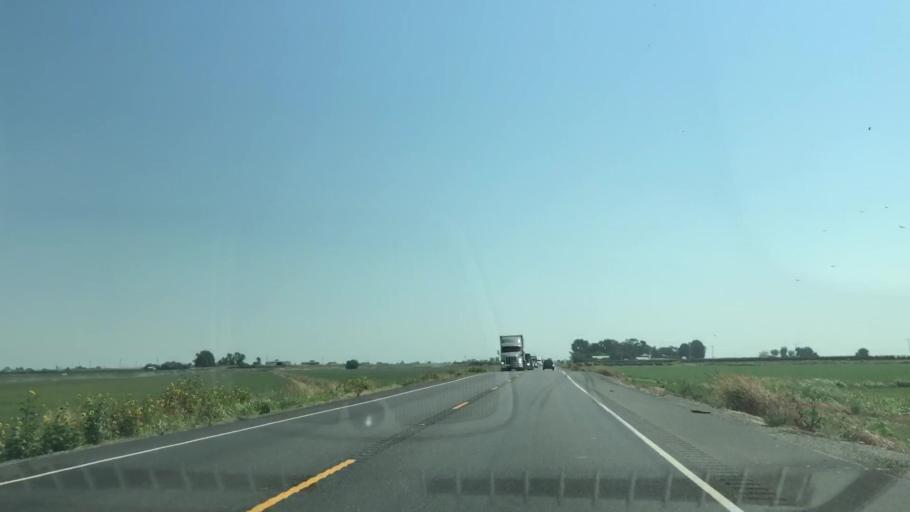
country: US
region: California
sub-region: Solano County
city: Rio Vista
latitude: 38.1429
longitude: -121.6343
